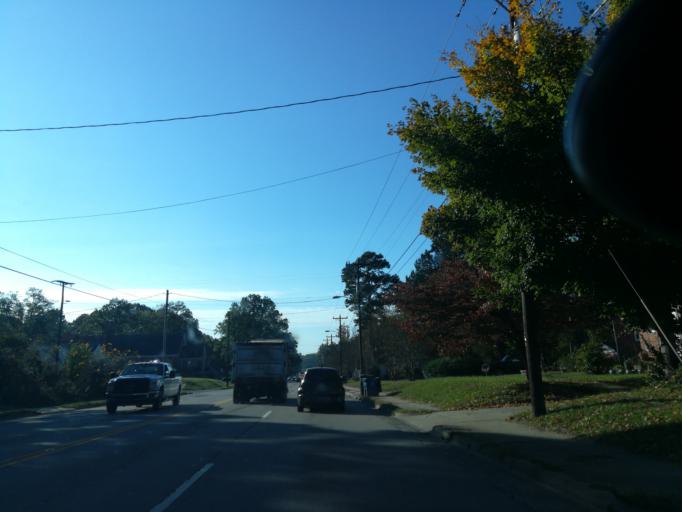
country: US
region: North Carolina
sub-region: Durham County
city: Durham
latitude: 36.0262
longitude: -78.8898
